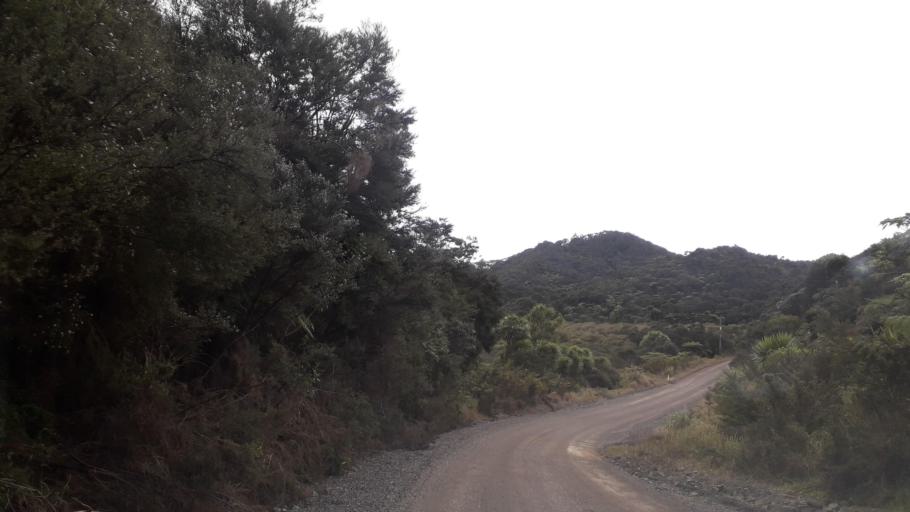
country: NZ
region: Northland
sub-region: Far North District
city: Paihia
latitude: -35.3299
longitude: 174.2317
